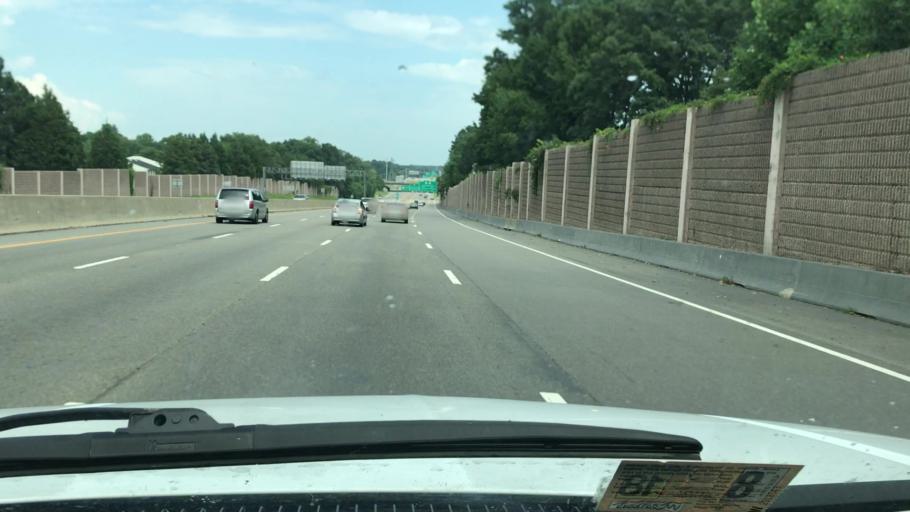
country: US
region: Virginia
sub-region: Chesterfield County
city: Bensley
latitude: 37.4426
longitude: -77.4482
